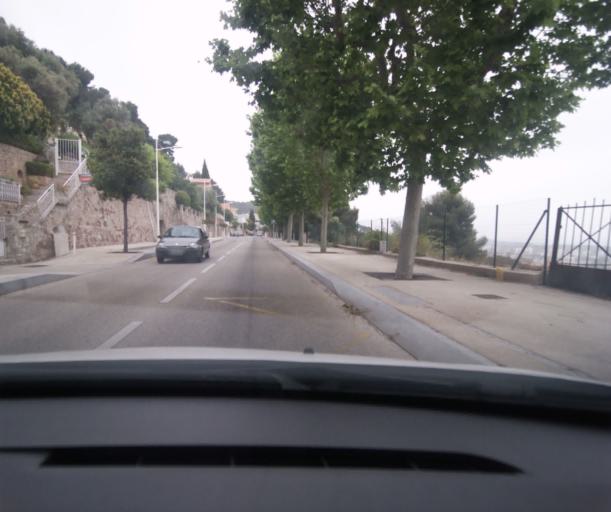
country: FR
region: Provence-Alpes-Cote d'Azur
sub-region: Departement du Var
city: La Valette-du-Var
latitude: 43.1350
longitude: 5.9623
